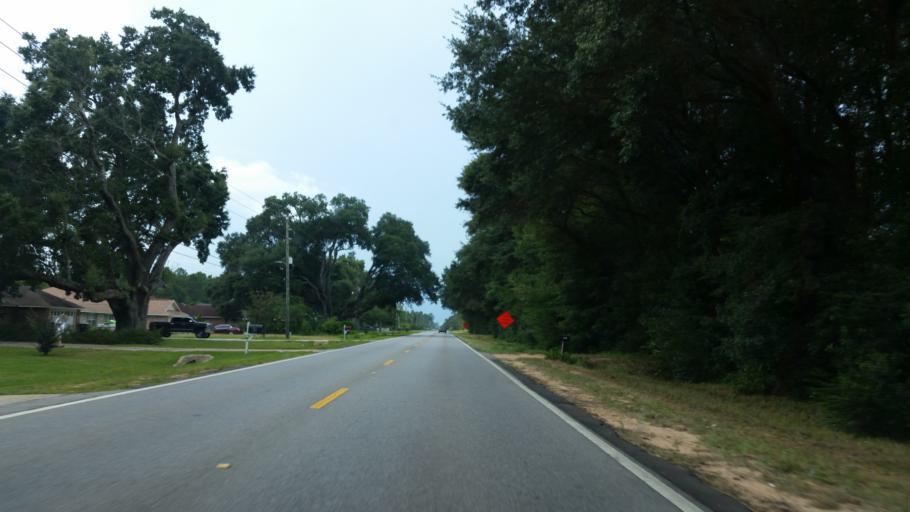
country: US
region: Florida
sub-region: Santa Rosa County
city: Pace
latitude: 30.6276
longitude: -87.1665
